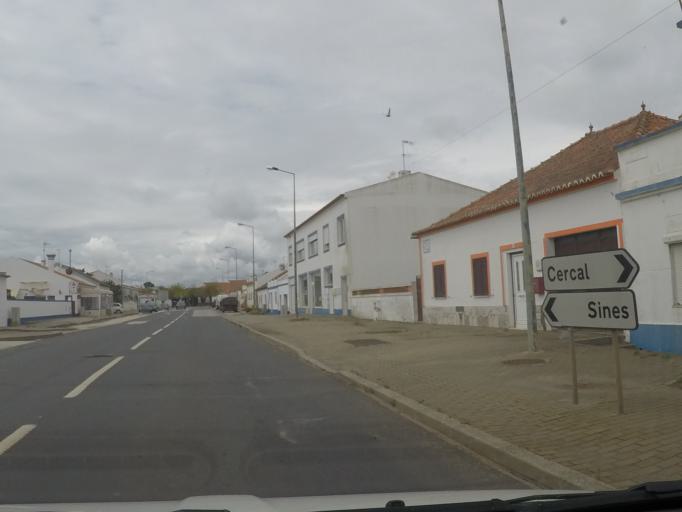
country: PT
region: Setubal
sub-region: Sines
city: Porto Covo
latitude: 37.8652
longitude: -8.7195
